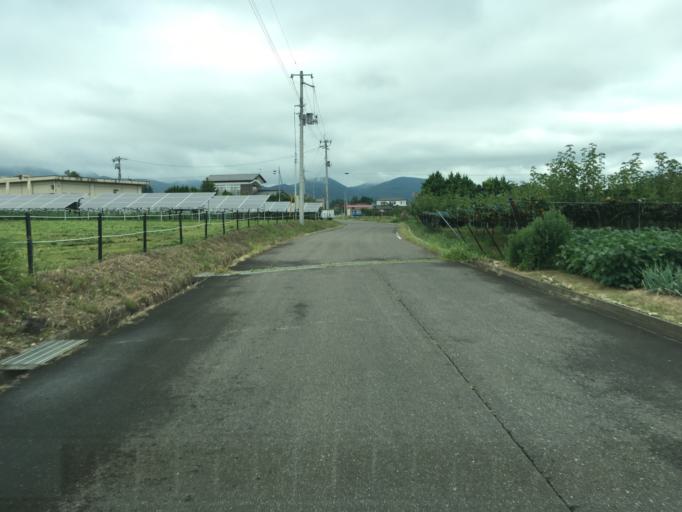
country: JP
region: Fukushima
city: Fukushima-shi
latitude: 37.7711
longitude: 140.4069
